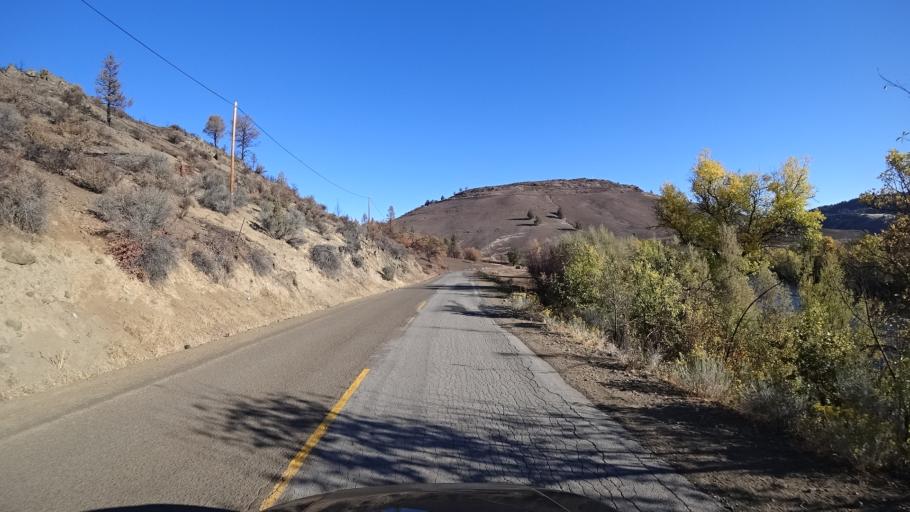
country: US
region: California
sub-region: Siskiyou County
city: Montague
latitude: 41.9155
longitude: -122.4619
